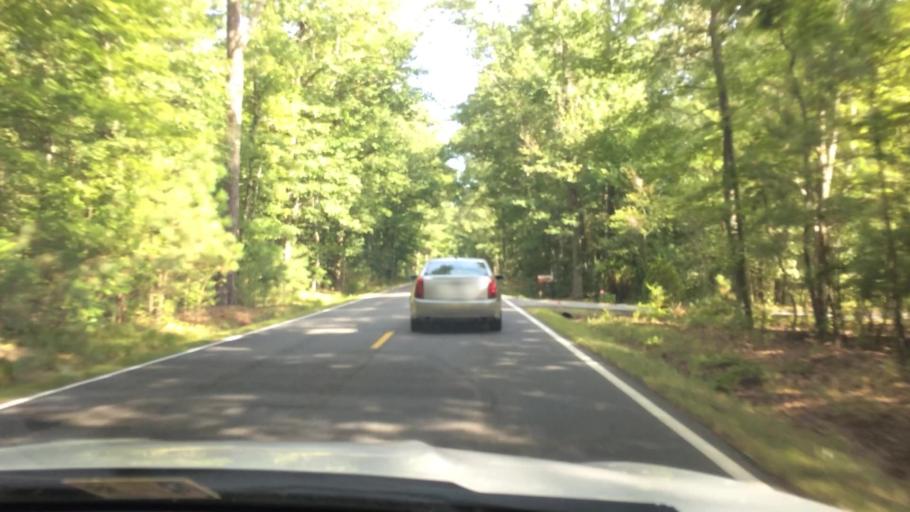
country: US
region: Virginia
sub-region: King William County
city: West Point
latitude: 37.4974
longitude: -76.8188
